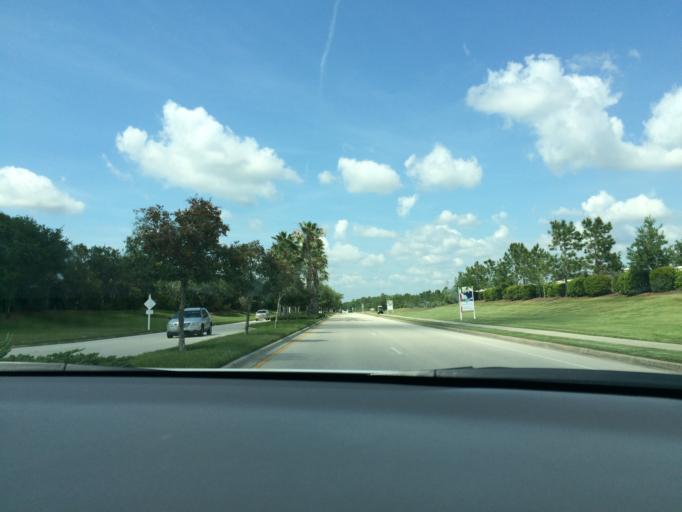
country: US
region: Florida
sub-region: Sarasota County
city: The Meadows
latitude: 27.4102
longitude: -82.3995
